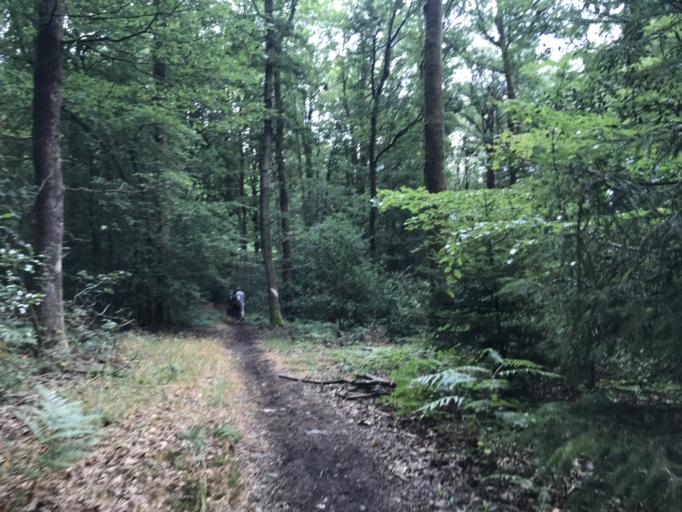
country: FR
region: Champagne-Ardenne
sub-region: Departement des Ardennes
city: Montherme
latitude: 49.8924
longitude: 4.7501
